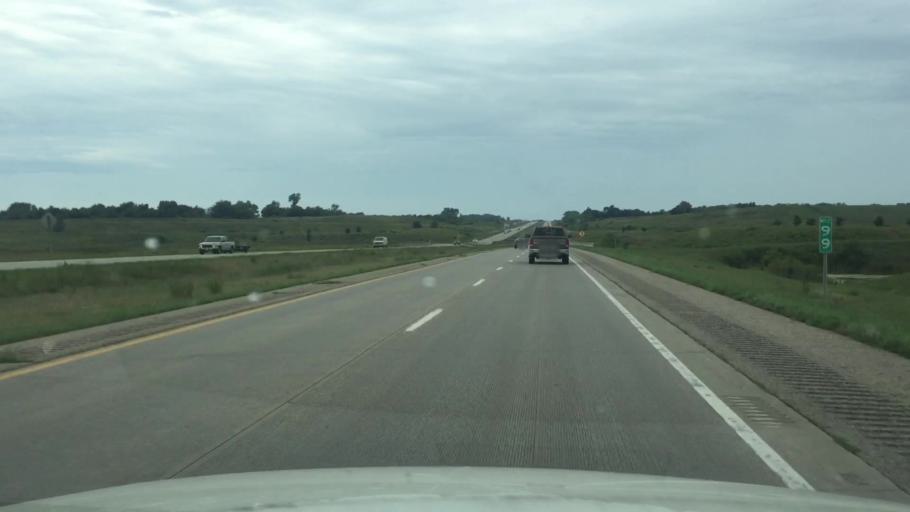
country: US
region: Iowa
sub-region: Warren County
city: Norwalk
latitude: 41.5142
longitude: -93.6778
